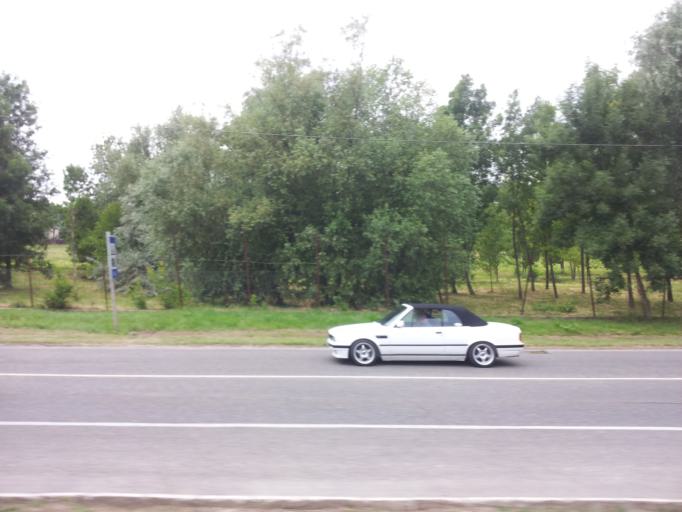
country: HU
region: Veszprem
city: Balatonalmadi
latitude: 47.0199
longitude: 18.0079
